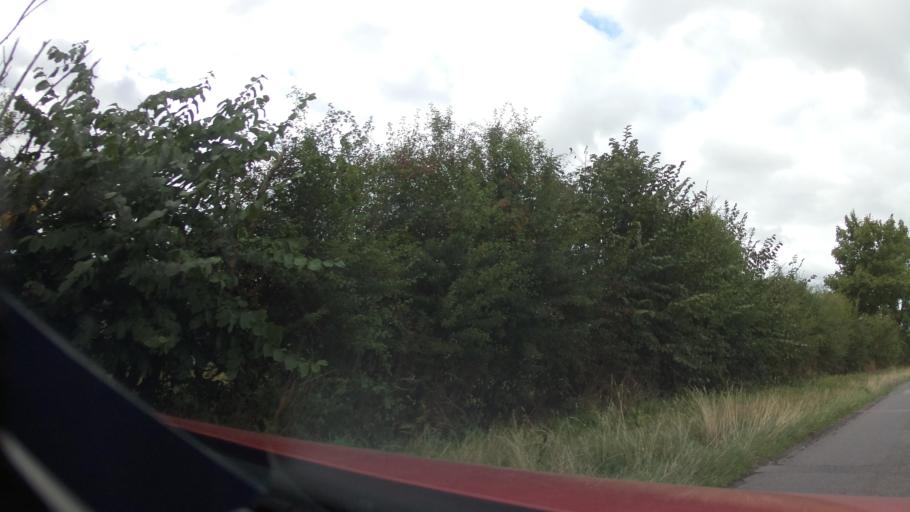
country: GB
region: England
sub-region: Nottinghamshire
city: East Leake
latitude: 52.8220
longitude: -1.1759
